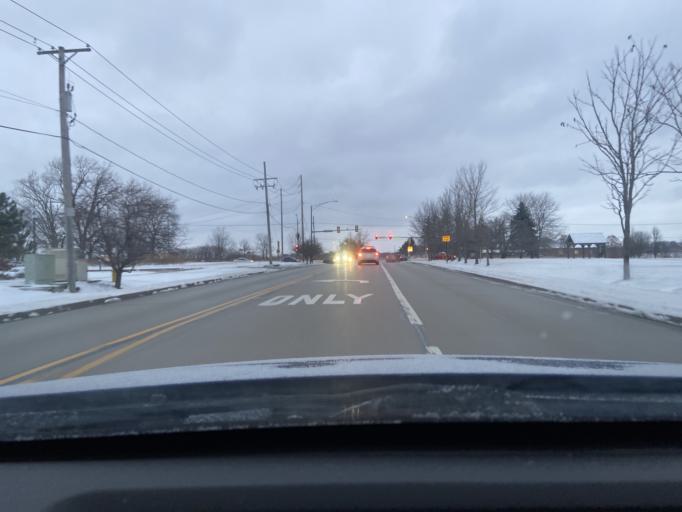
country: US
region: Illinois
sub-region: Lake County
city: Third Lake
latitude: 42.3595
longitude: -88.0241
